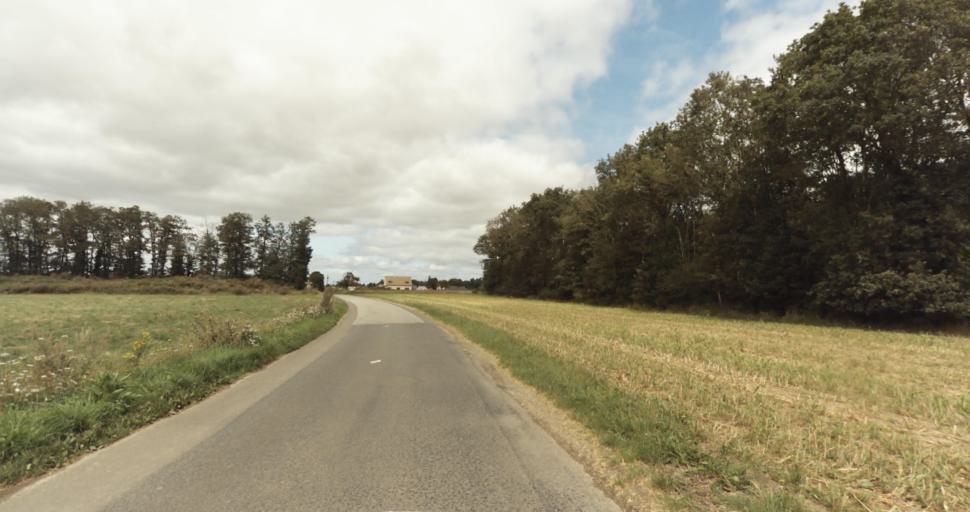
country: FR
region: Haute-Normandie
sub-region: Departement de l'Eure
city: Evreux
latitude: 48.9290
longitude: 1.2029
